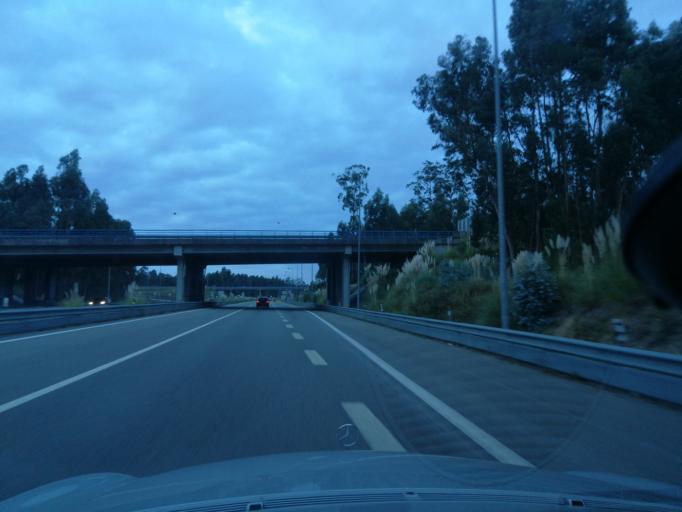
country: PT
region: Aveiro
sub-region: Estarreja
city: Beduido
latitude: 40.7824
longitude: -8.5620
